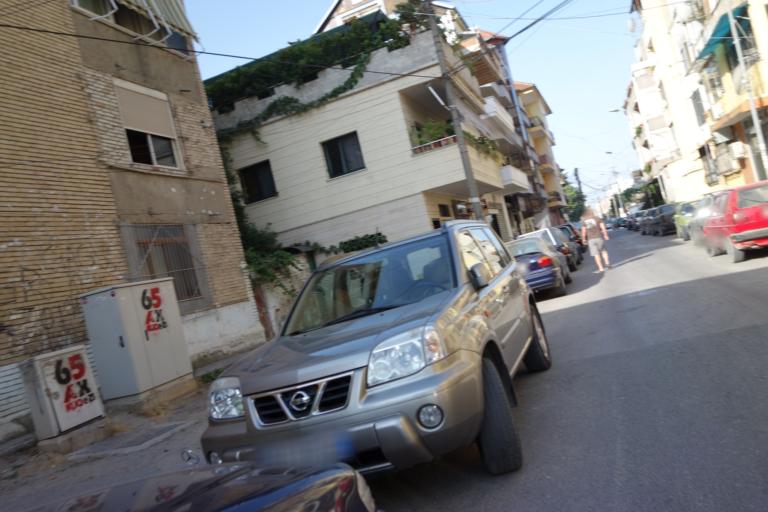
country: AL
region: Tirane
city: Tirana
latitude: 41.3354
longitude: 19.8322
